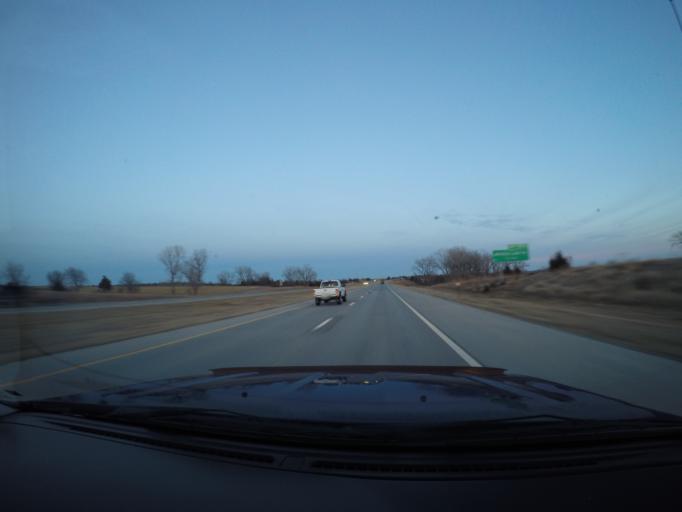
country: US
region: Kansas
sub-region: Dickinson County
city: Chapman
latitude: 38.9950
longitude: -96.9581
